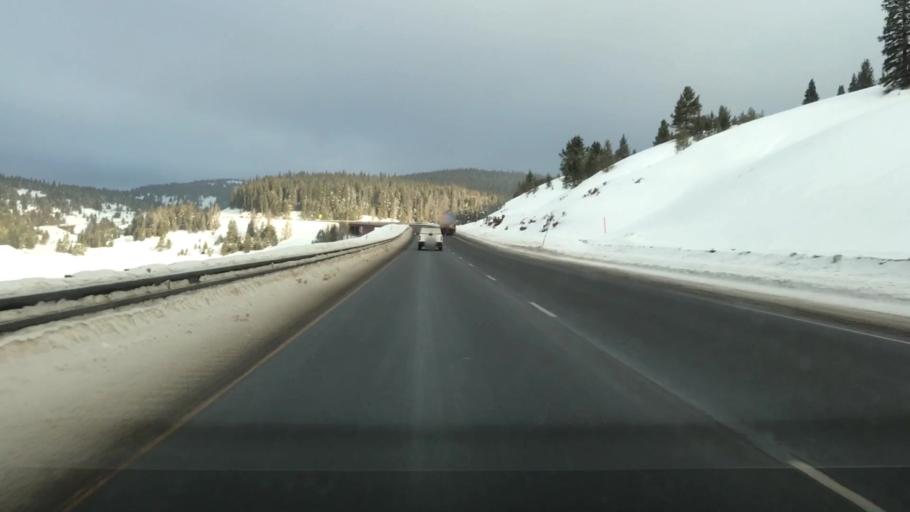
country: US
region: Colorado
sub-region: Summit County
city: Frisco
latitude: 39.5121
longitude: -106.2036
